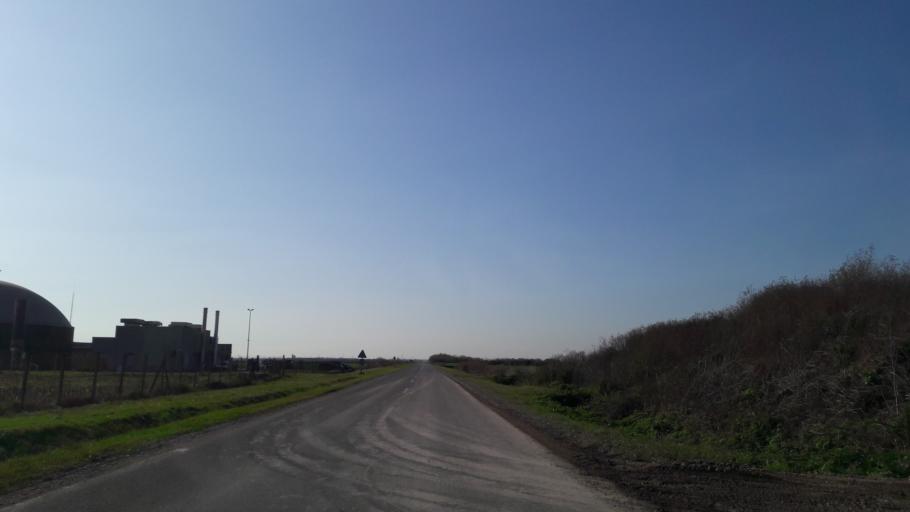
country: HR
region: Osjecko-Baranjska
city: Tenja
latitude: 45.4834
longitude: 18.7185
